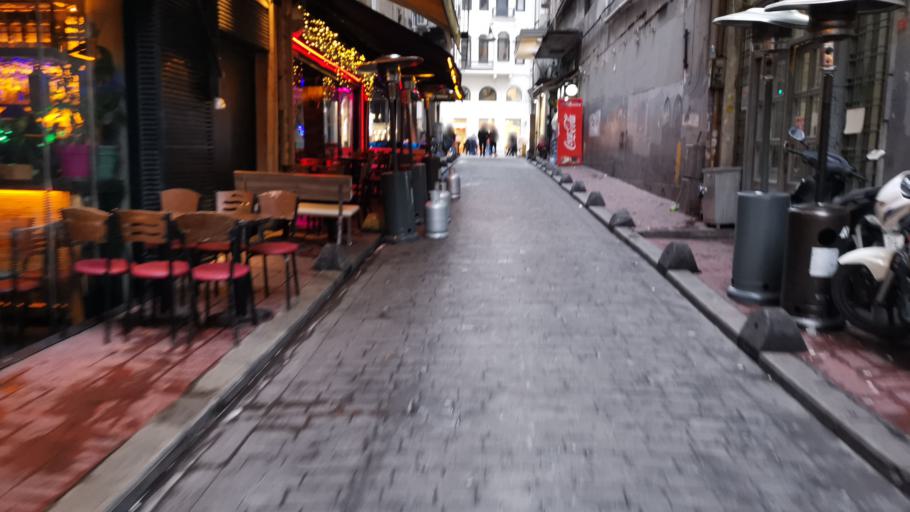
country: TR
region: Istanbul
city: Eminoenue
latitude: 41.0345
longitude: 28.9785
